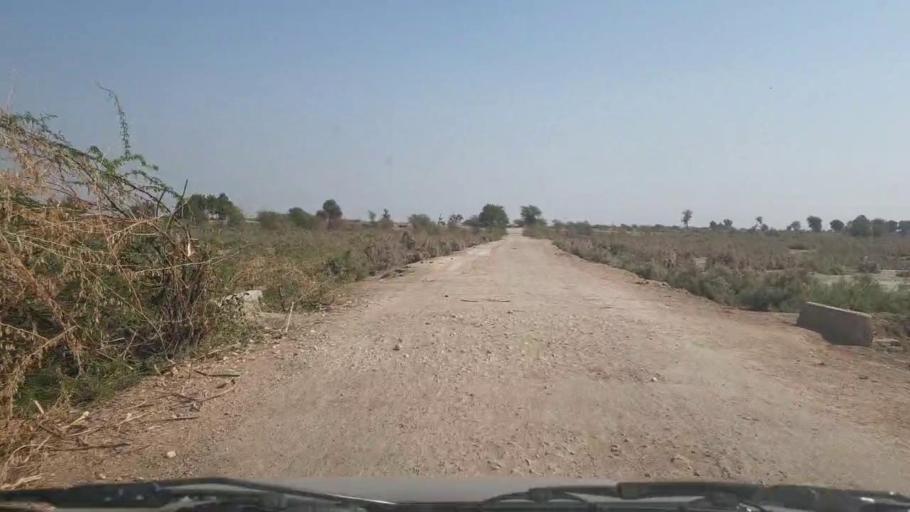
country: PK
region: Sindh
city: Samaro
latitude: 25.2412
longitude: 69.3726
